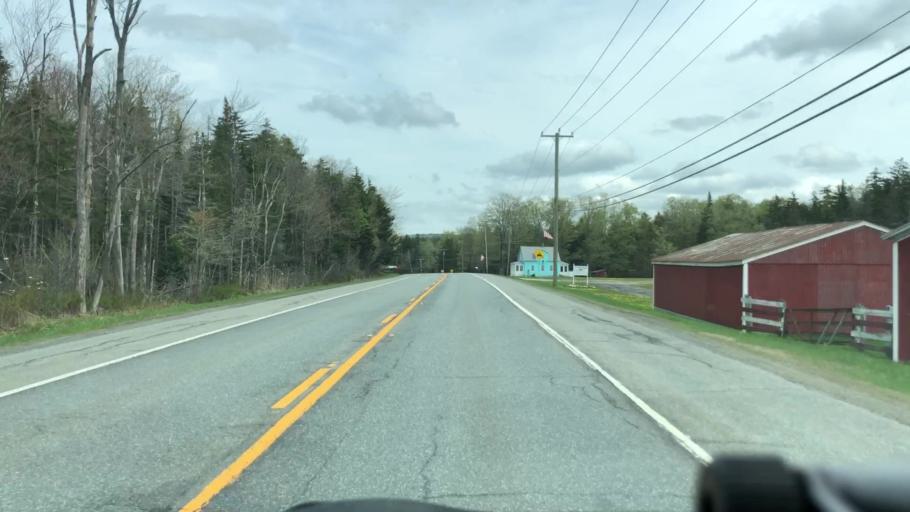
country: US
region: Massachusetts
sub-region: Berkshire County
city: Hinsdale
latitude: 42.5086
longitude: -73.0874
